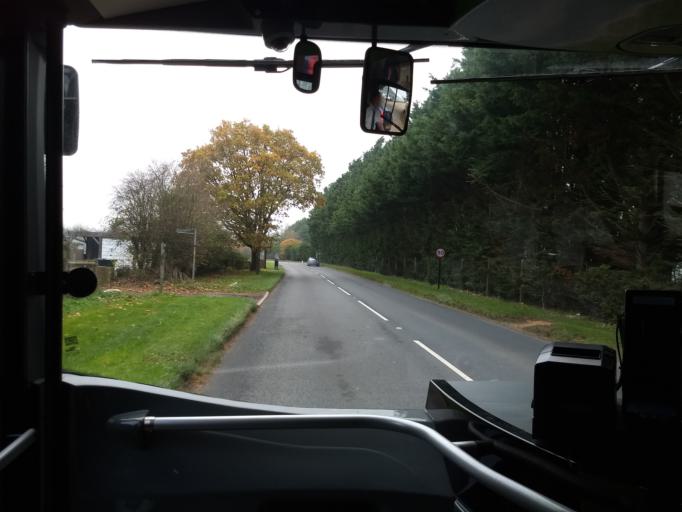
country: GB
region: England
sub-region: Isle of Wight
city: Newchurch
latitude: 50.6559
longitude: -1.2239
